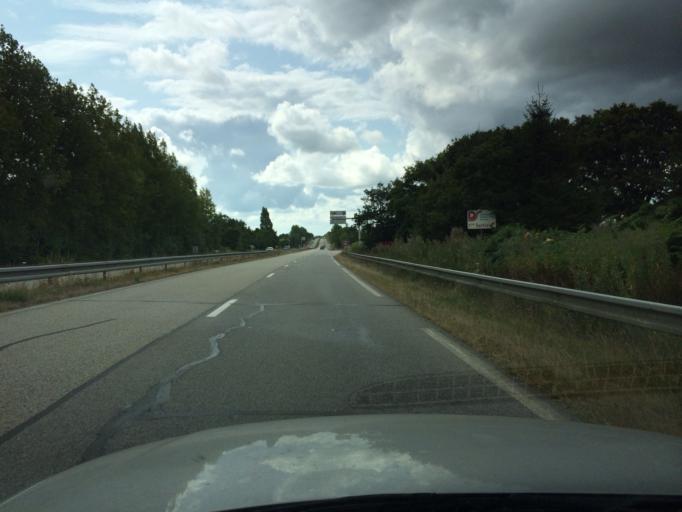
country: FR
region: Lower Normandy
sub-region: Departement de la Manche
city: Valognes
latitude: 49.5163
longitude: -1.4963
